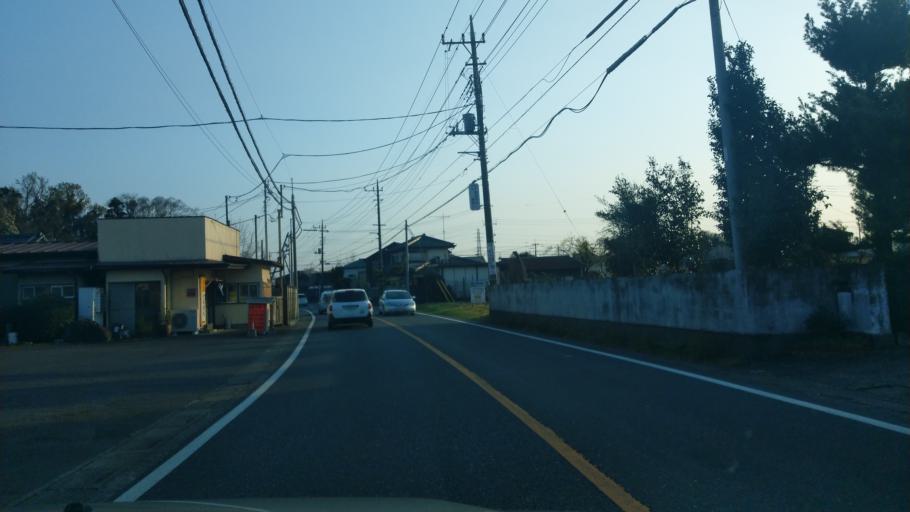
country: JP
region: Saitama
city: Ageoshimo
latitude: 36.0027
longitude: 139.6048
